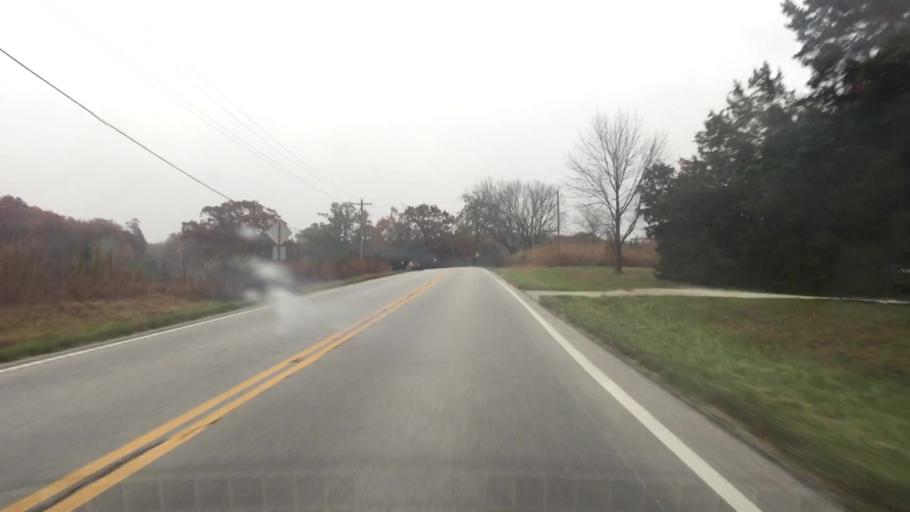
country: US
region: Missouri
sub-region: Callaway County
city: Fulton
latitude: 38.8791
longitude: -92.0849
